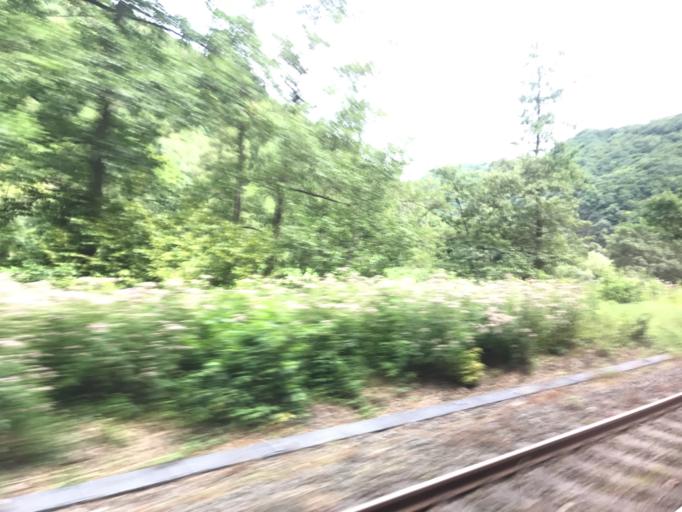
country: DE
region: Rheinland-Pfalz
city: Seelbach
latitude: 50.3157
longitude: 7.8592
